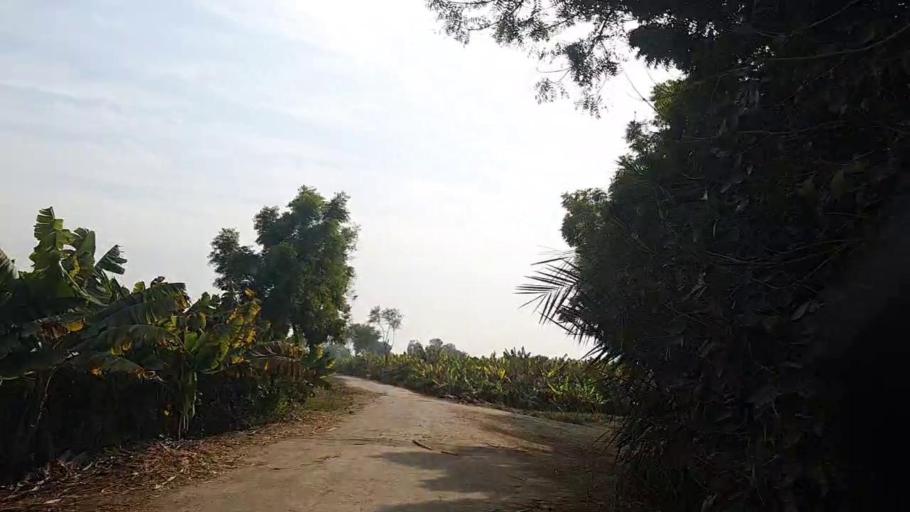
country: PK
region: Sindh
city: Daur
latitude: 26.3949
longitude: 68.2015
